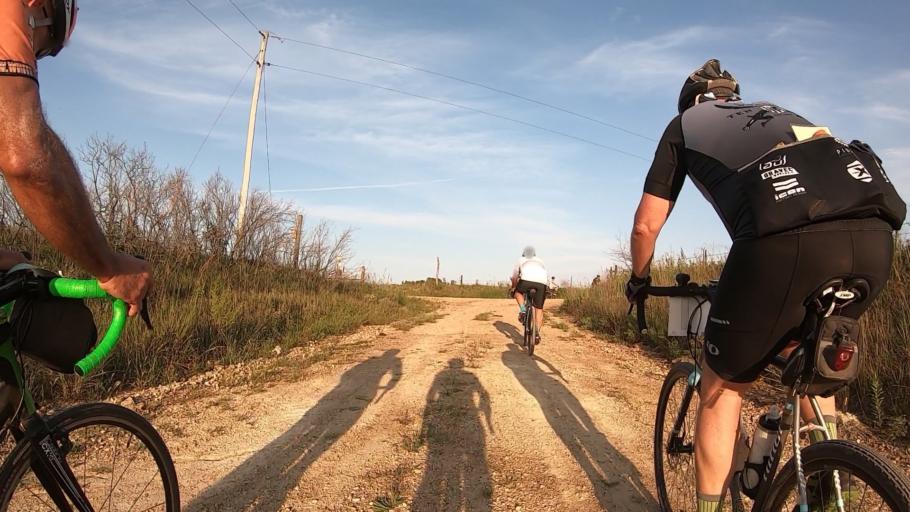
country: US
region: Kansas
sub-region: Marshall County
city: Blue Rapids
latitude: 39.7656
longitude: -96.7127
